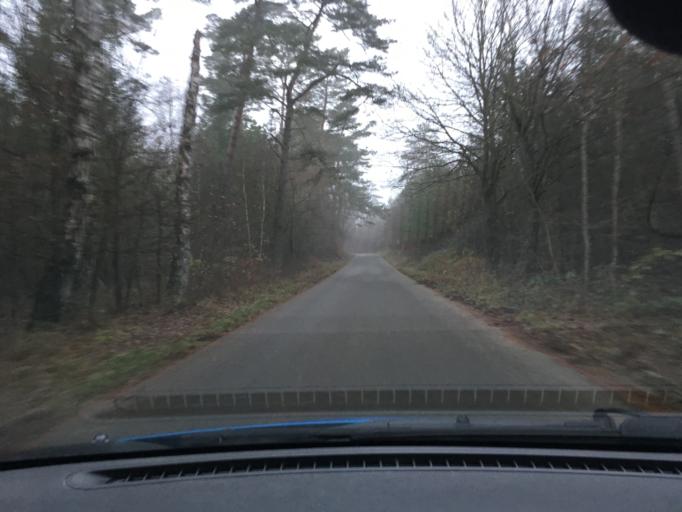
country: DE
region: Lower Saxony
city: Oldendorf
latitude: 53.1498
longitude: 10.1898
